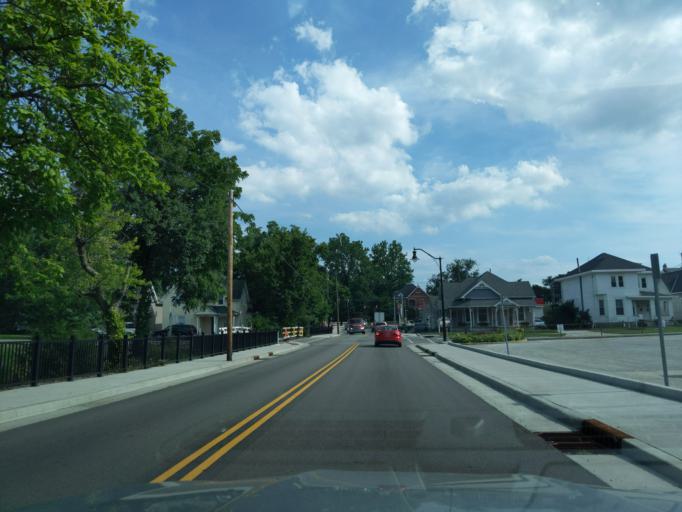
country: US
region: Indiana
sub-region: Decatur County
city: Greensburg
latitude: 39.3382
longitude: -85.4796
